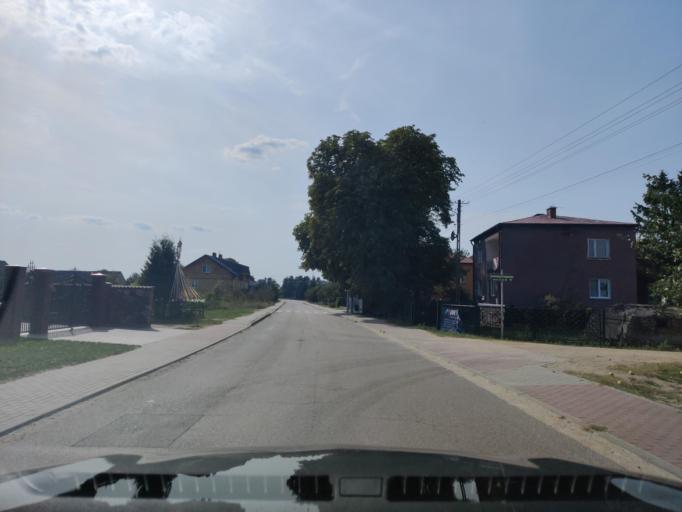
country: PL
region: Masovian Voivodeship
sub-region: Powiat wyszkowski
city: Rzasnik
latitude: 52.7650
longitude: 21.3627
